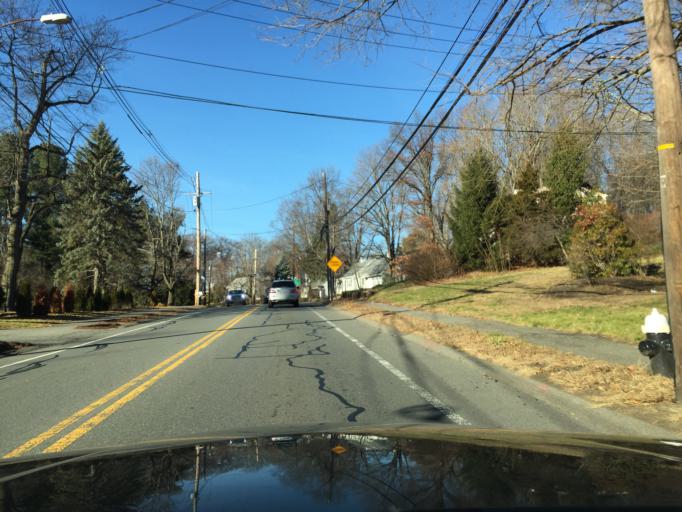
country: US
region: Massachusetts
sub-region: Middlesex County
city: Lexington
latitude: 42.4431
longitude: -71.1946
